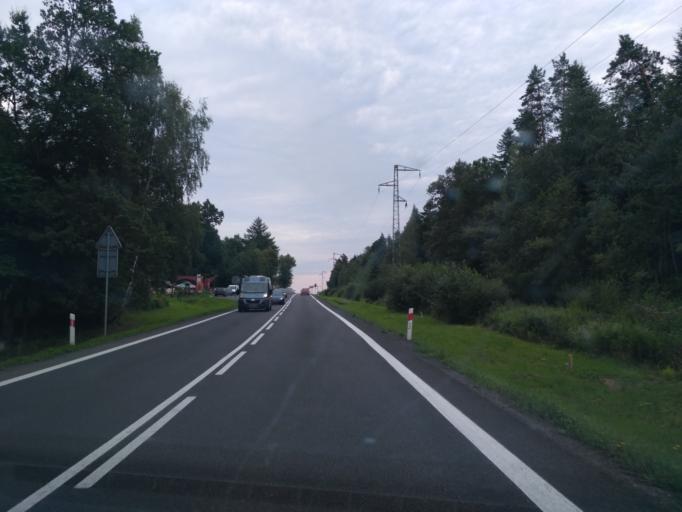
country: PL
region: Subcarpathian Voivodeship
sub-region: Powiat sanocki
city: Zagorz
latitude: 49.5064
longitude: 22.2946
